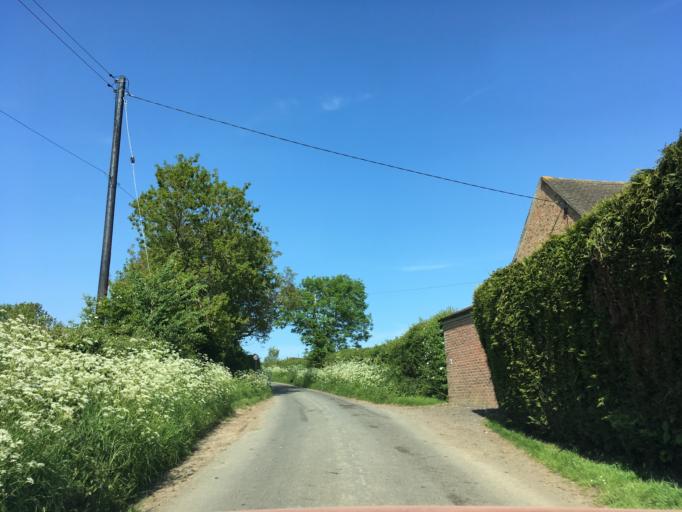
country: GB
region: England
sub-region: Gloucestershire
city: Dursley
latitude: 51.7199
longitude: -2.3882
